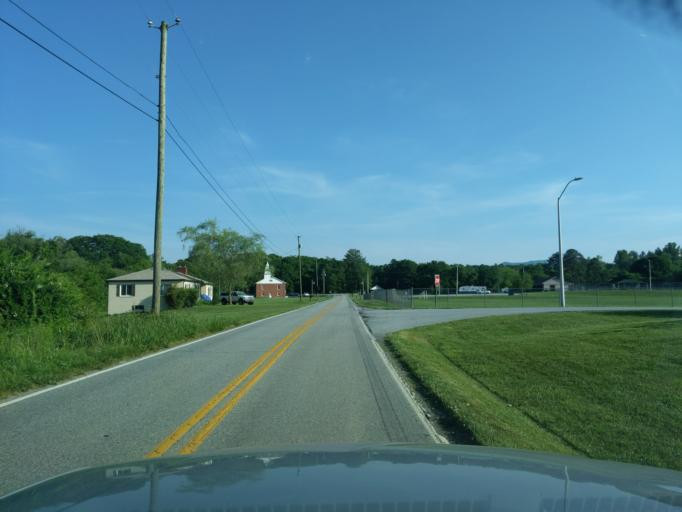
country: US
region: North Carolina
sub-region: Buncombe County
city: Fairview
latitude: 35.4821
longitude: -82.4360
